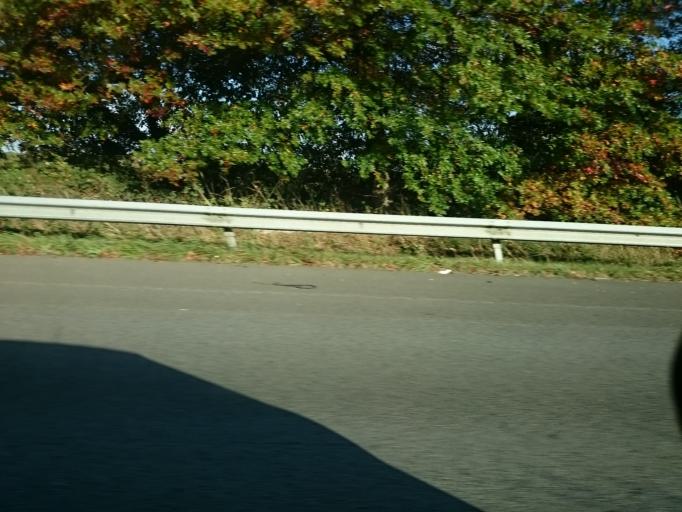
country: FR
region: Pays de la Loire
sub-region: Departement de la Loire-Atlantique
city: Nozay
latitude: 47.5516
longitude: -1.6323
